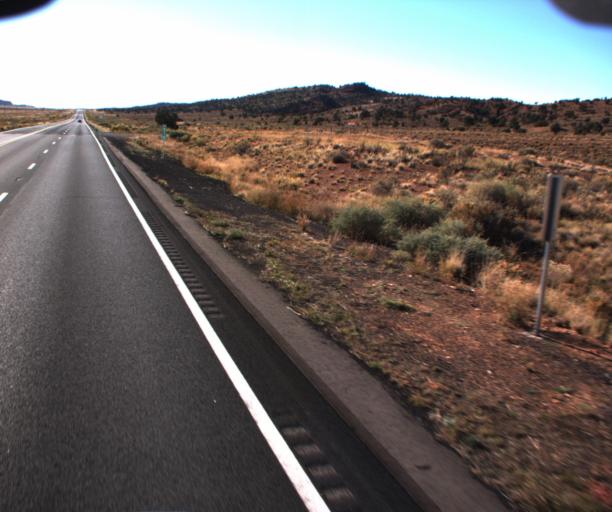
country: US
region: Arizona
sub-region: Coconino County
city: LeChee
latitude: 36.4544
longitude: -111.5622
